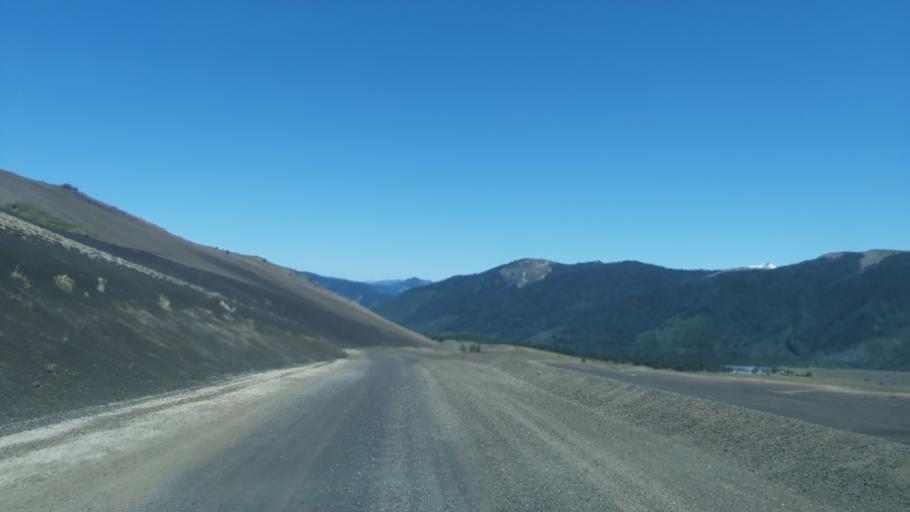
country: CL
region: Araucania
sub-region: Provincia de Cautin
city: Vilcun
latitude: -38.4048
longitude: -71.5436
